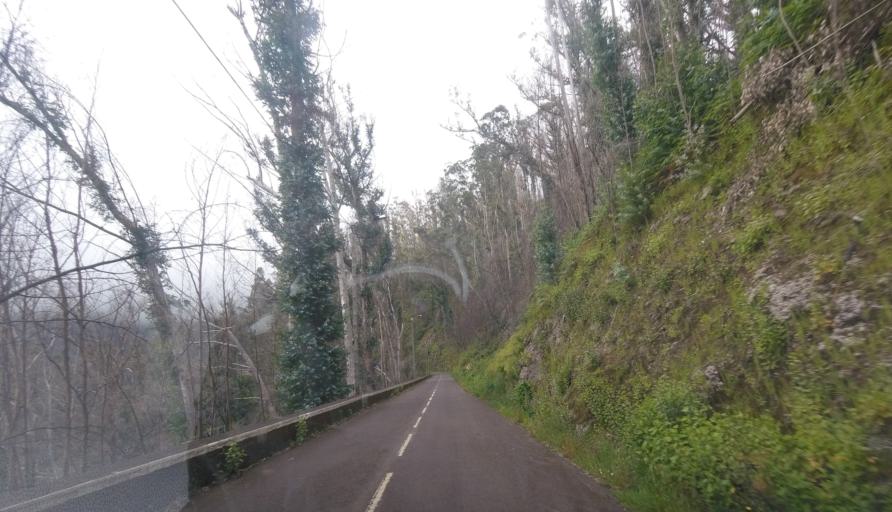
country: PT
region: Madeira
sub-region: Funchal
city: Nossa Senhora do Monte
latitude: 32.6817
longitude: -16.8909
